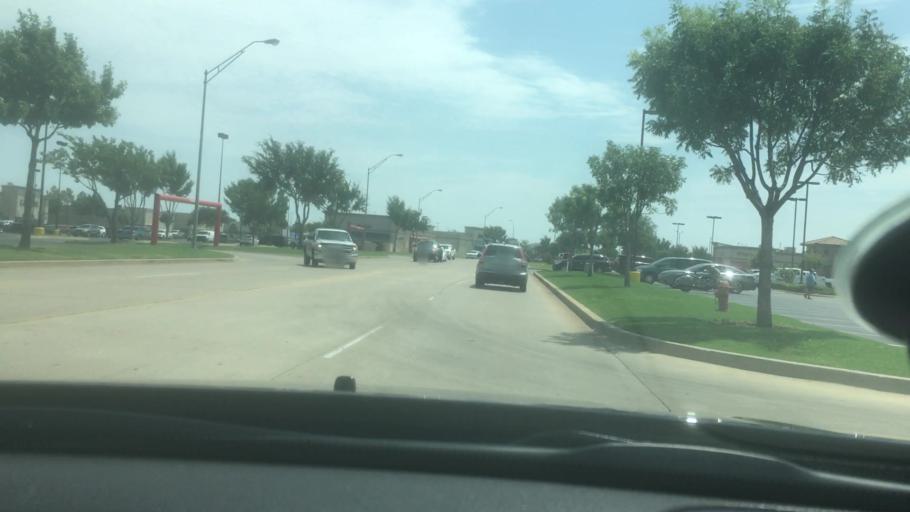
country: US
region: Oklahoma
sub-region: Oklahoma County
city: Bethany
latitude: 35.4619
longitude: -97.6271
